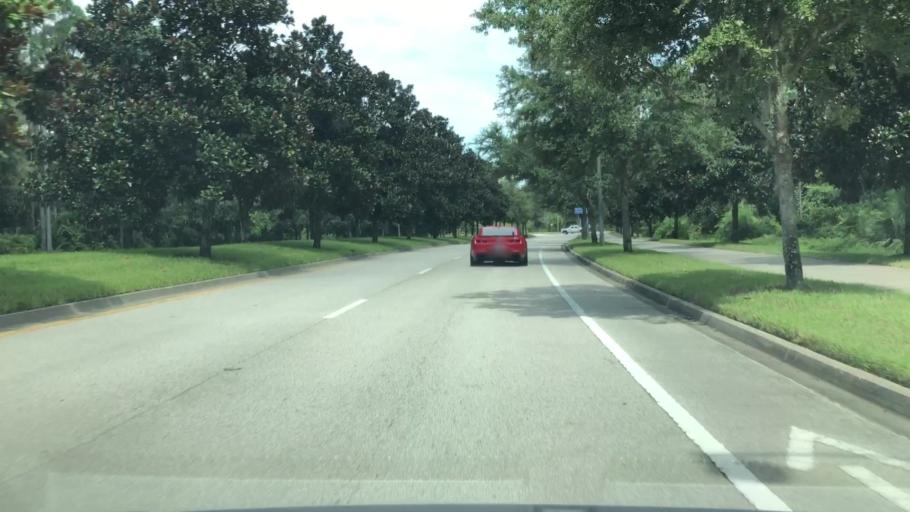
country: US
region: Florida
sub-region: Saint Johns County
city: Palm Valley
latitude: 30.1229
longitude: -81.4208
